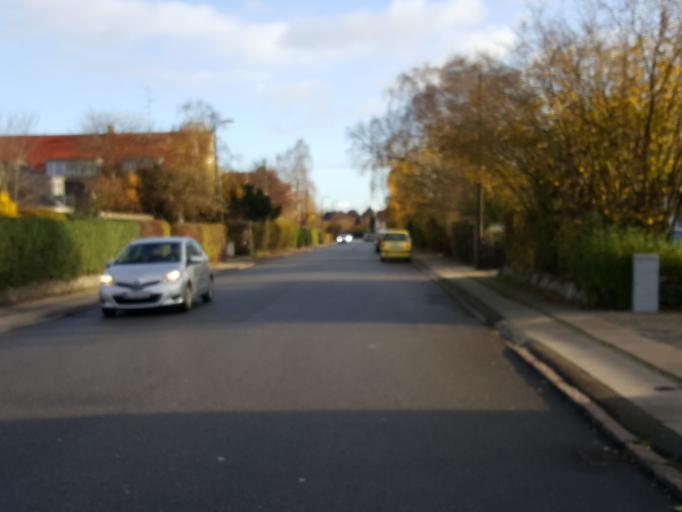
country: DK
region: Capital Region
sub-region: Tarnby Kommune
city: Tarnby
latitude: 55.6434
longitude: 12.6123
